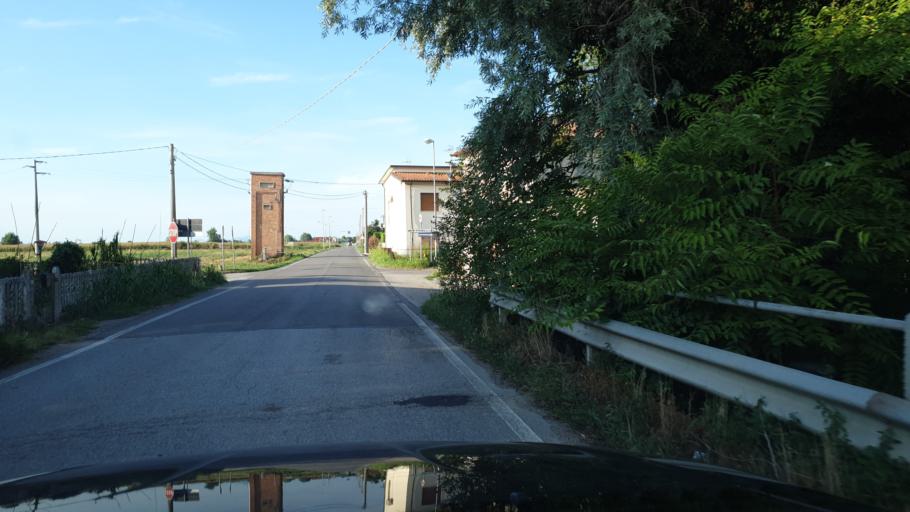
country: IT
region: Veneto
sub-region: Provincia di Rovigo
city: Fiesso Umbertiano
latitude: 44.9441
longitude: 11.6200
